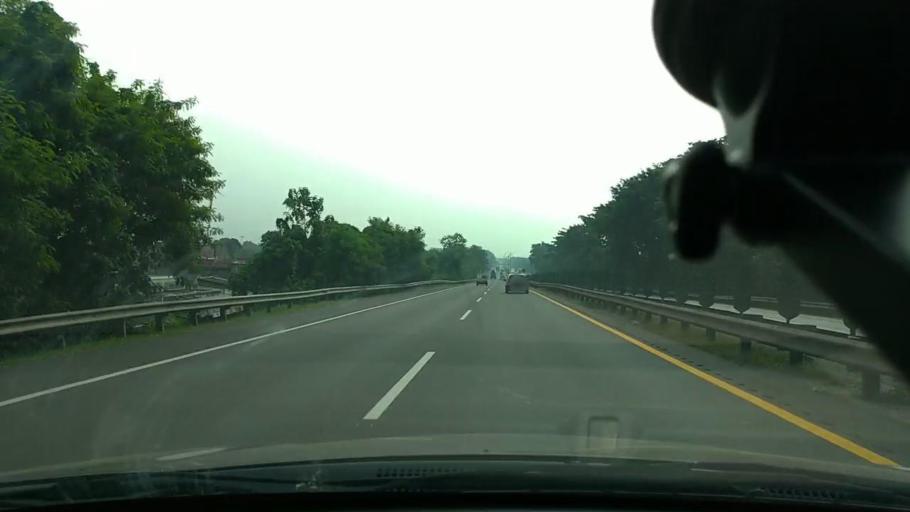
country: ID
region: Banten
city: Serang
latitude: -6.0917
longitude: 106.1547
